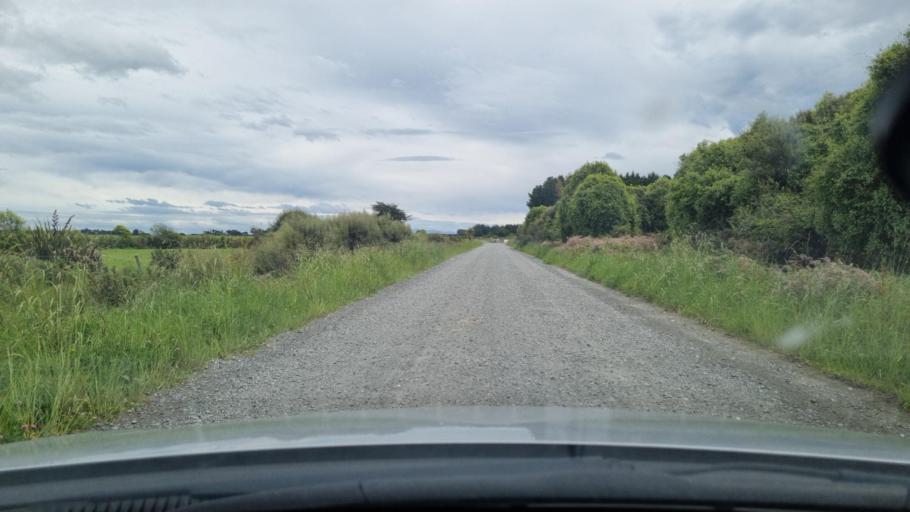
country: NZ
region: Southland
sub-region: Invercargill City
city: Invercargill
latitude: -46.4063
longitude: 168.2763
